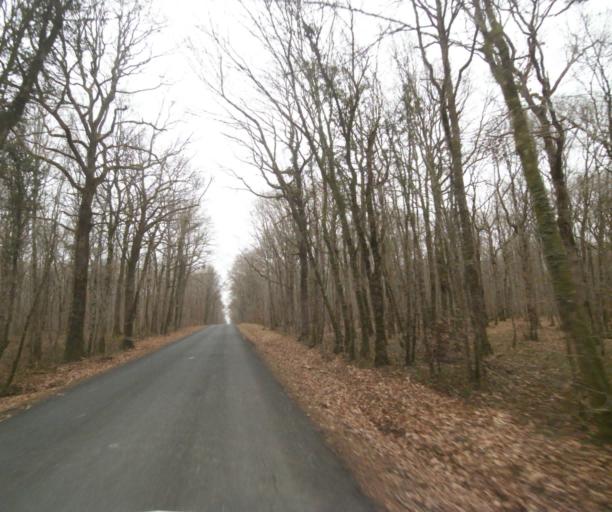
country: FR
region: Champagne-Ardenne
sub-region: Departement de la Haute-Marne
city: Bienville
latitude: 48.5524
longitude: 5.0009
